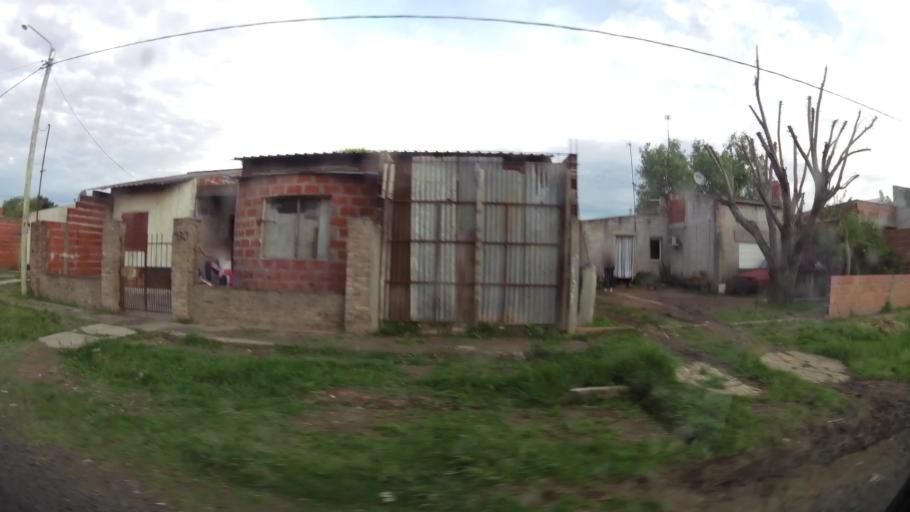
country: AR
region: Buenos Aires
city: San Nicolas de los Arroyos
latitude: -33.3188
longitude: -60.2462
